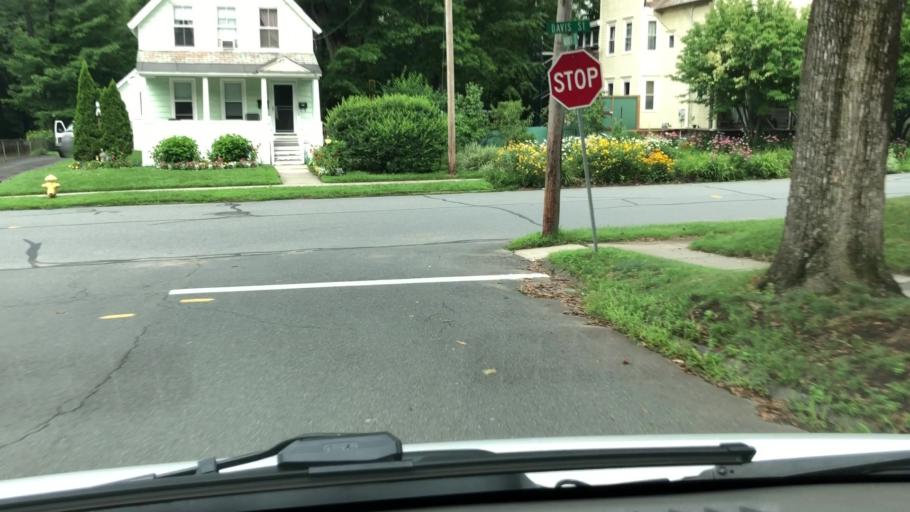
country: US
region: Massachusetts
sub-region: Franklin County
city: Greenfield
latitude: 42.5961
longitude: -72.6004
